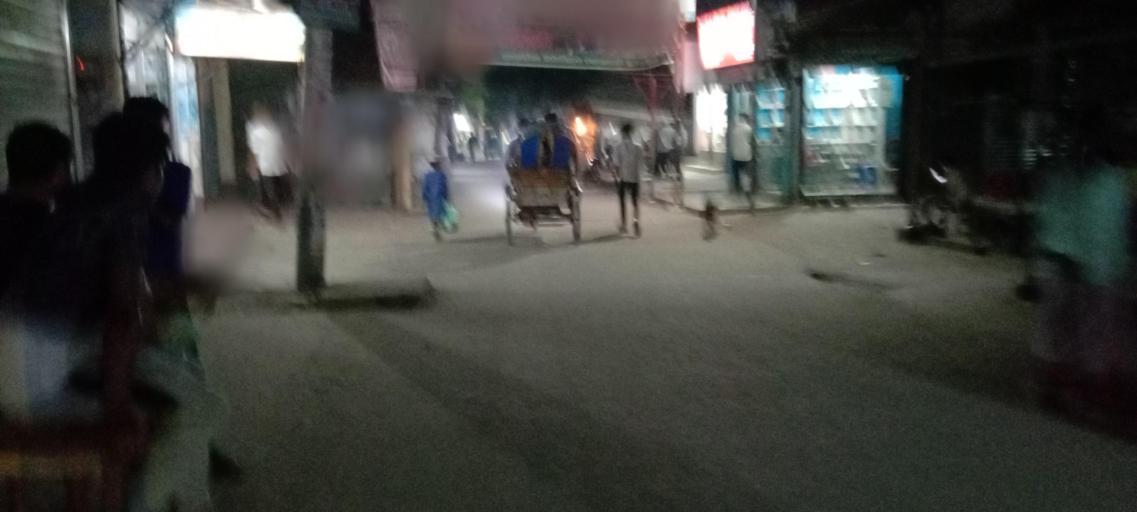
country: BD
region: Dhaka
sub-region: Dhaka
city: Dhaka
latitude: 23.6596
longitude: 90.3609
